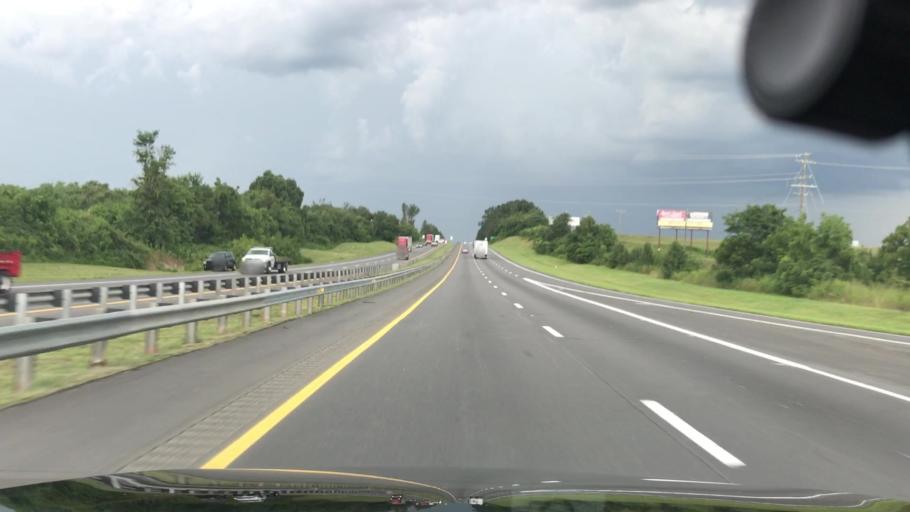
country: US
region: North Carolina
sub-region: Iredell County
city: Statesville
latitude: 35.8164
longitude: -80.8607
